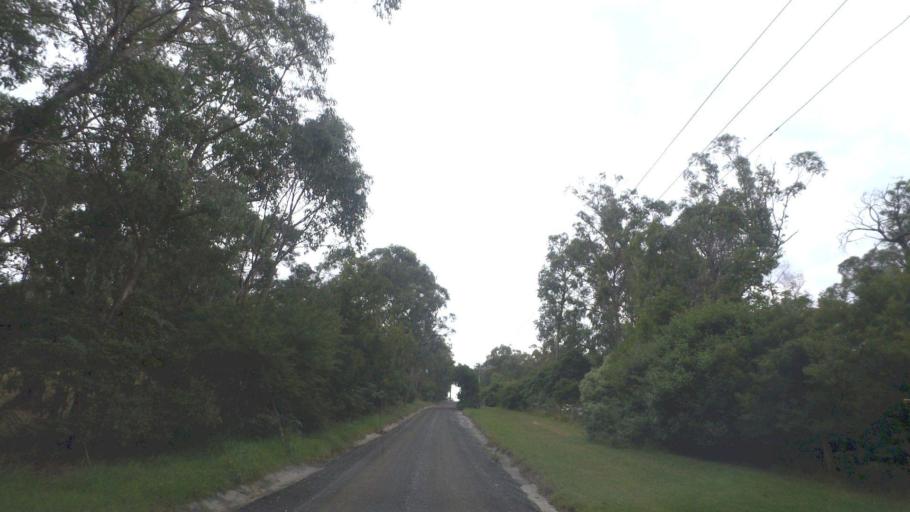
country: AU
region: Victoria
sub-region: Yarra Ranges
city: Mount Evelyn
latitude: -37.7618
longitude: 145.3754
